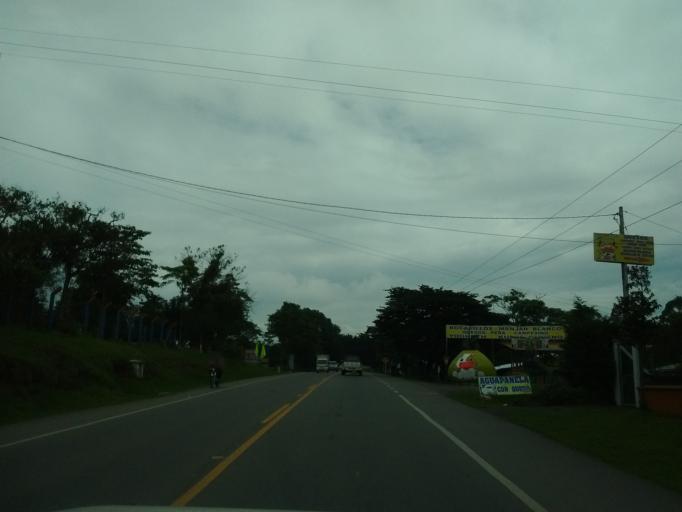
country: CO
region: Cauca
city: Cajibio
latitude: 2.5685
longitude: -76.5618
